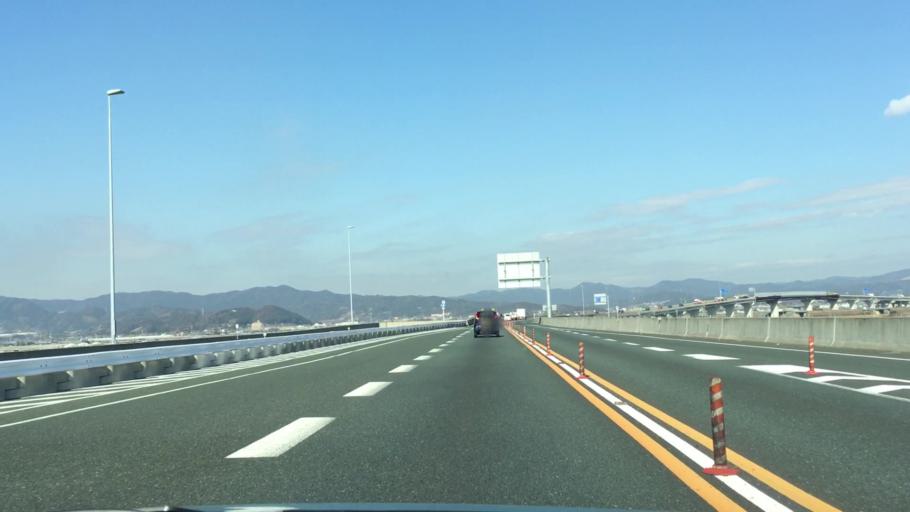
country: JP
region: Aichi
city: Kozakai-cho
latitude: 34.7898
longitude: 137.3317
